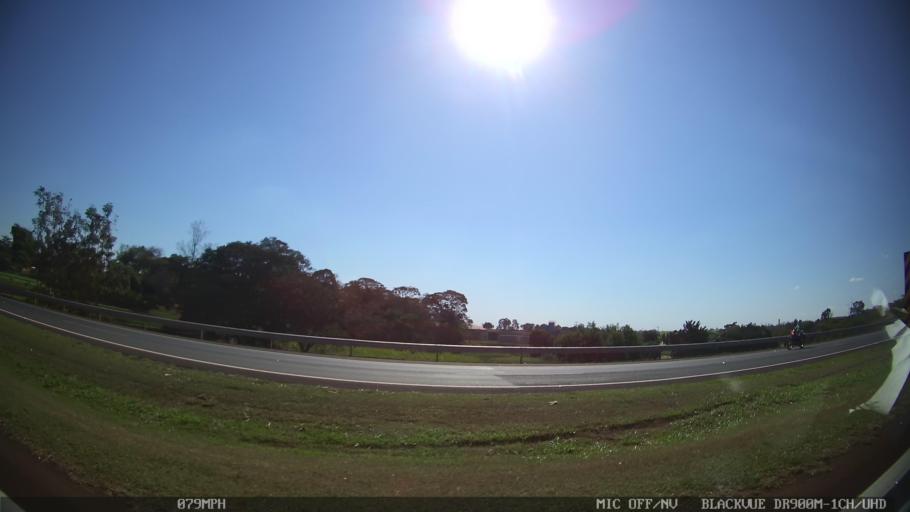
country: BR
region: Sao Paulo
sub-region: Ribeirao Preto
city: Ribeirao Preto
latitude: -21.1076
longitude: -47.8117
